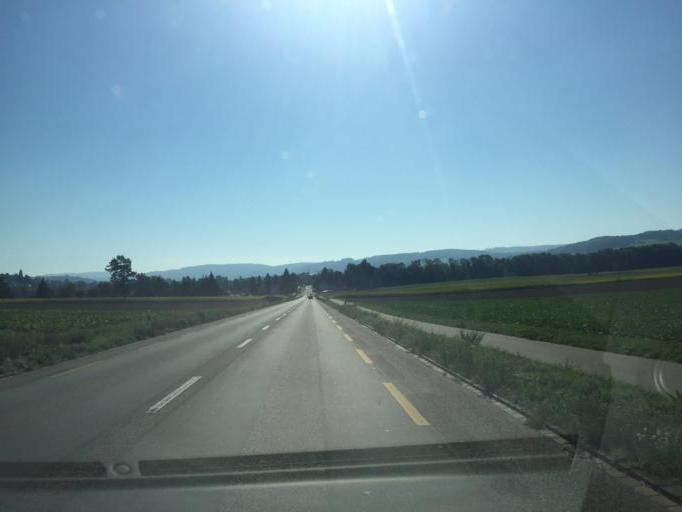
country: CH
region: Thurgau
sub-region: Frauenfeld District
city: Wagenhausen
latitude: 47.6644
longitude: 8.8333
